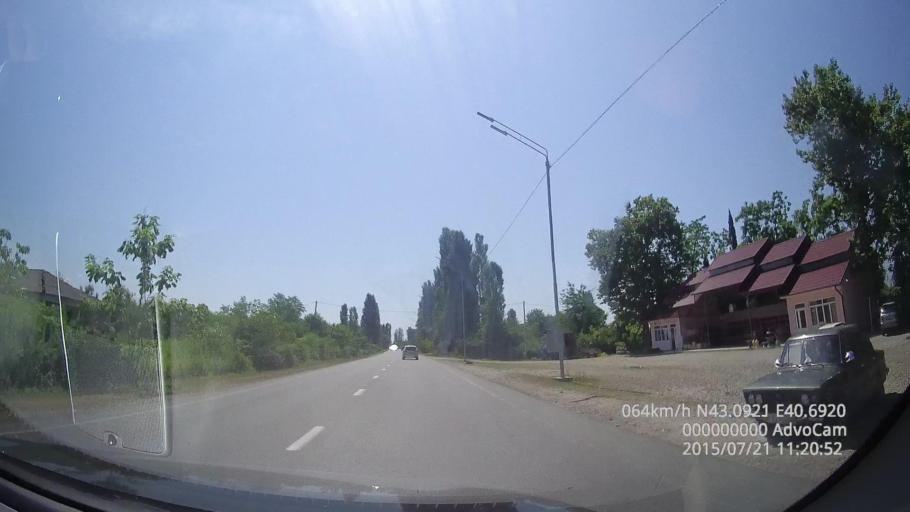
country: GE
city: P'rimorsk'oe
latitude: 43.0919
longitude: 40.6923
